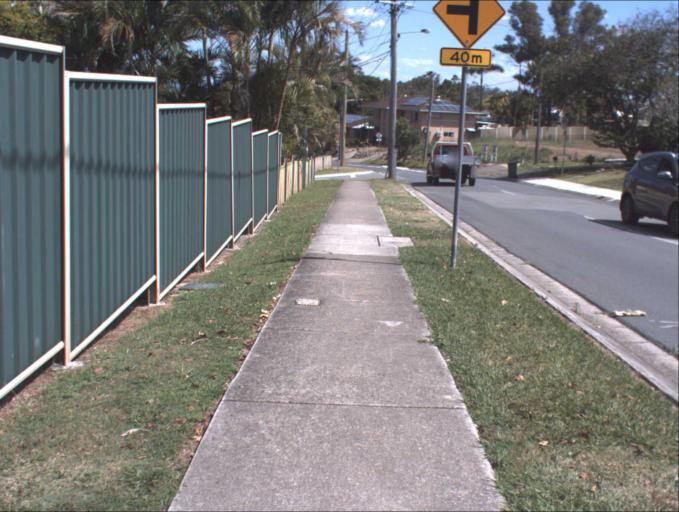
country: AU
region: Queensland
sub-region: Logan
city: Rochedale South
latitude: -27.5980
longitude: 153.1108
